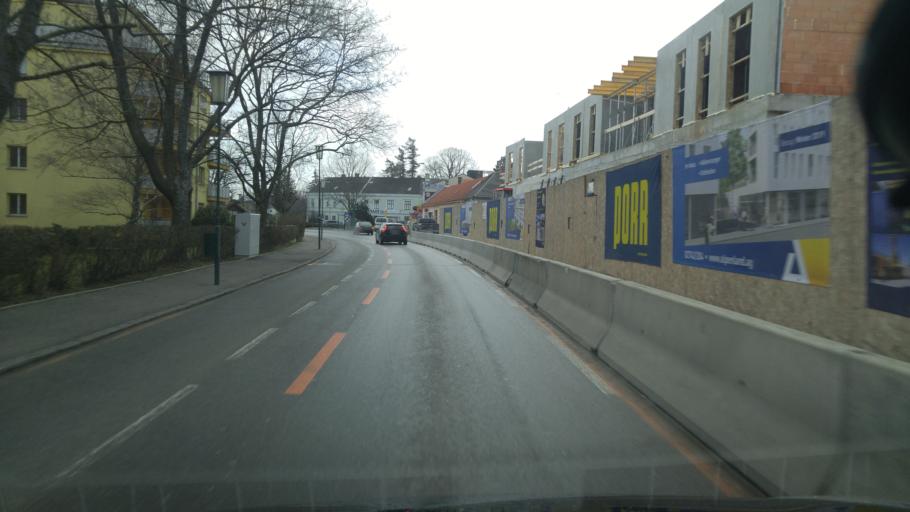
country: AT
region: Lower Austria
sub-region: Politischer Bezirk Baden
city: Bad Voslau
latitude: 47.9641
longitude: 16.2149
